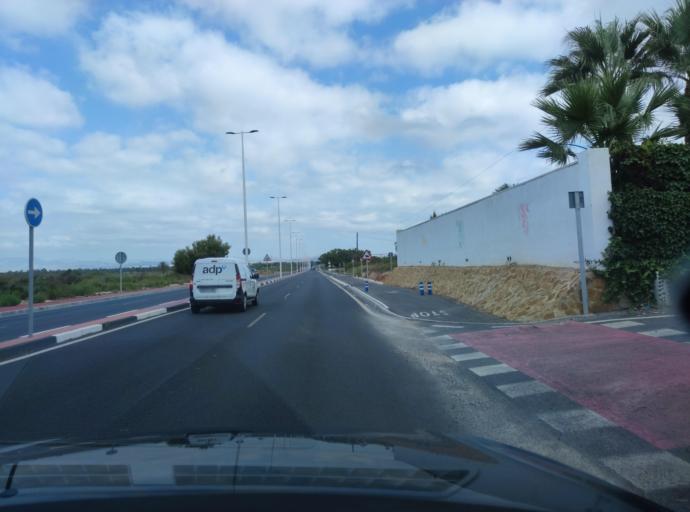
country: ES
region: Valencia
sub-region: Provincia de Alicante
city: Santa Pola
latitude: 38.2111
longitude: -0.5886
